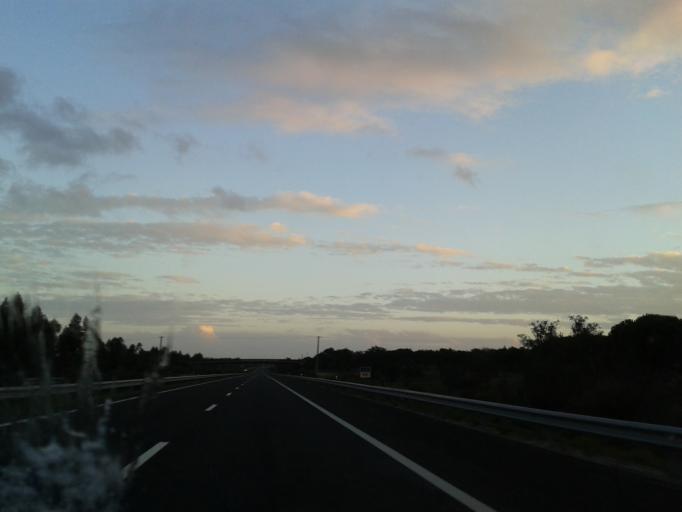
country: PT
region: Santarem
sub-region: Benavente
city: Poceirao
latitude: 38.8008
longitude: -8.6978
